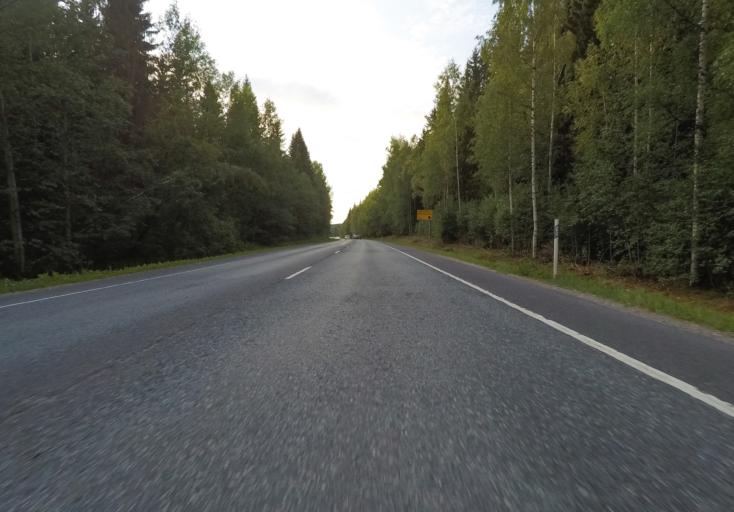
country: FI
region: Paijanne Tavastia
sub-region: Lahti
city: Lahti
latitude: 60.9930
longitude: 25.7266
